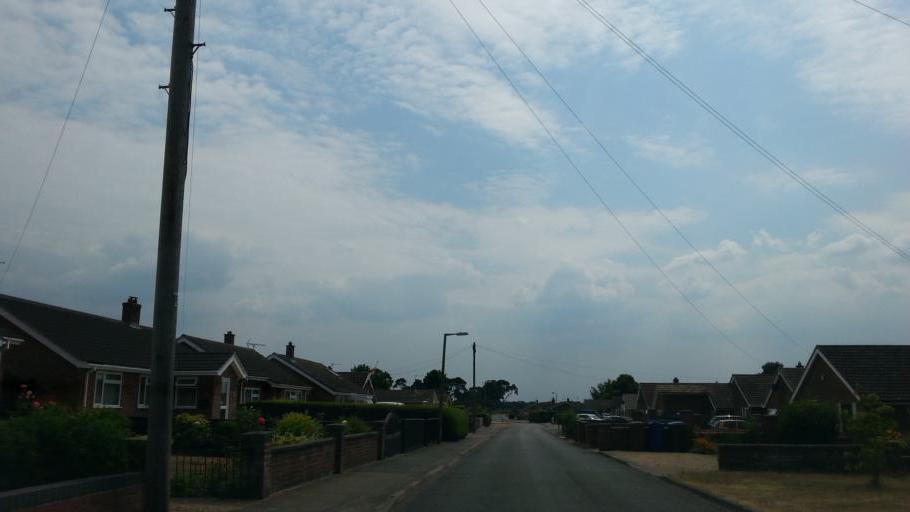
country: GB
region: England
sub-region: Suffolk
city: Lakenheath
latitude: 52.4146
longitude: 0.5296
